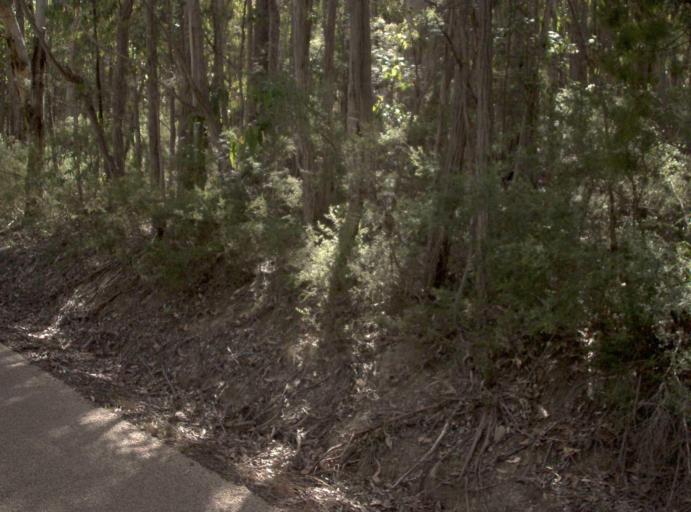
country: AU
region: Victoria
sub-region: East Gippsland
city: Lakes Entrance
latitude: -37.4532
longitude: 148.1250
